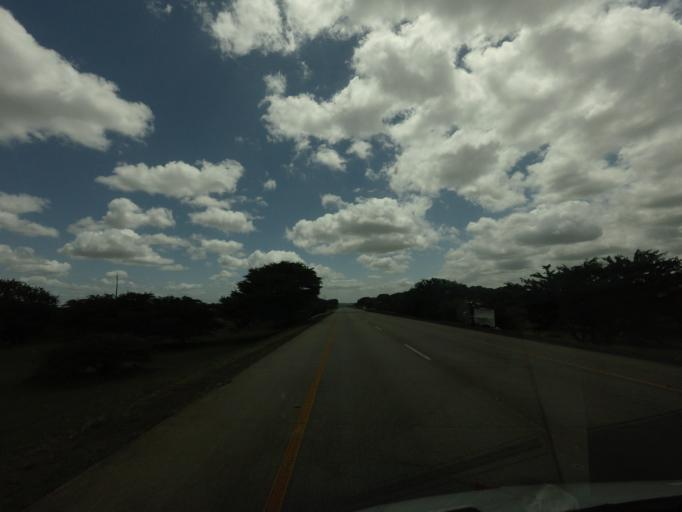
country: ZA
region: KwaZulu-Natal
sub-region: uMkhanyakude District Municipality
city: Mtubatuba
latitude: -28.4721
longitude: 32.1457
